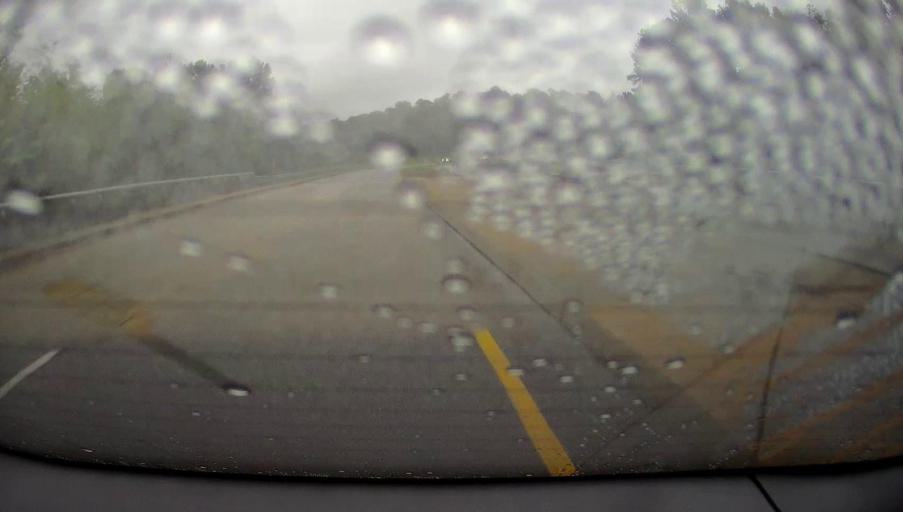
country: US
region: Georgia
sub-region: Houston County
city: Centerville
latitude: 32.5754
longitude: -83.6634
